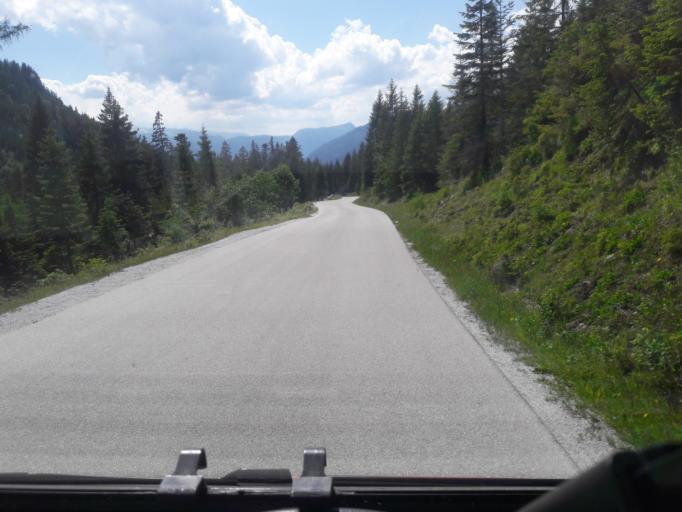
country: AT
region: Styria
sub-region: Politischer Bezirk Liezen
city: Tauplitz
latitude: 47.5845
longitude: 13.9644
